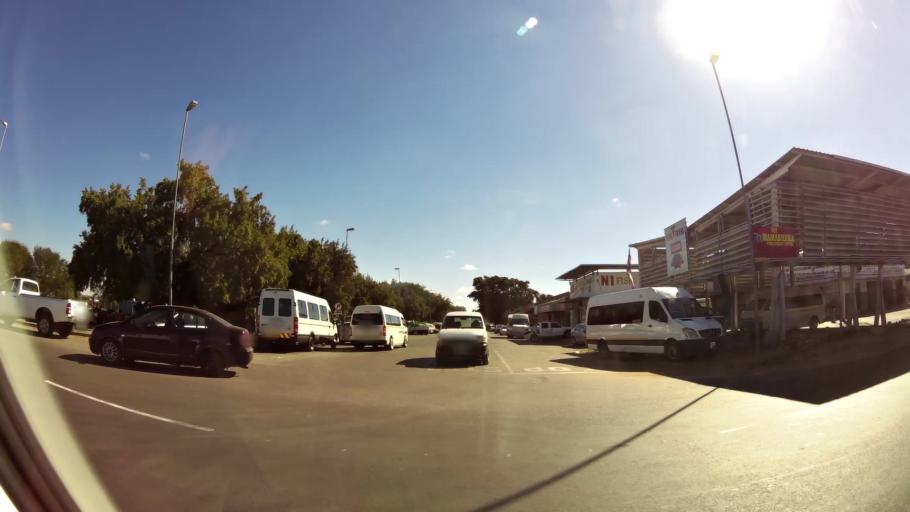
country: ZA
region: Limpopo
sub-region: Capricorn District Municipality
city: Polokwane
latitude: -23.9126
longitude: 29.4474
